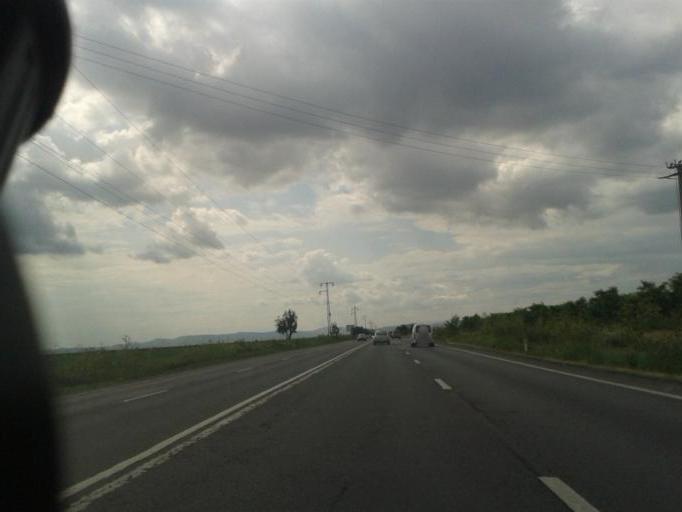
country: RO
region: Prahova
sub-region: Oras Baicoi
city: Tintea
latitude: 44.9970
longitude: 25.8969
